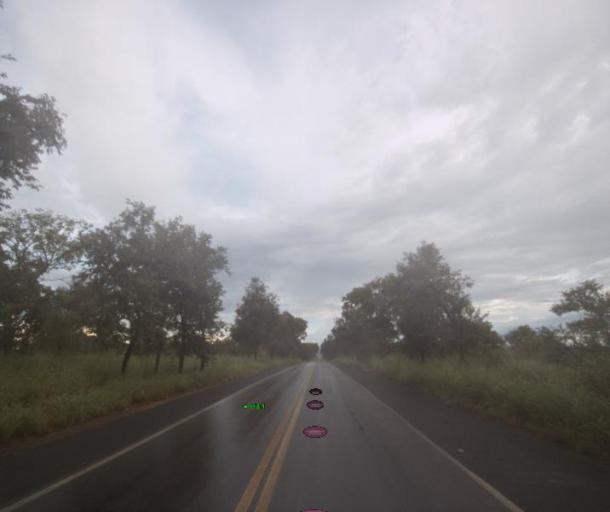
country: BR
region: Goias
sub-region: Porangatu
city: Porangatu
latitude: -13.8091
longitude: -49.0388
